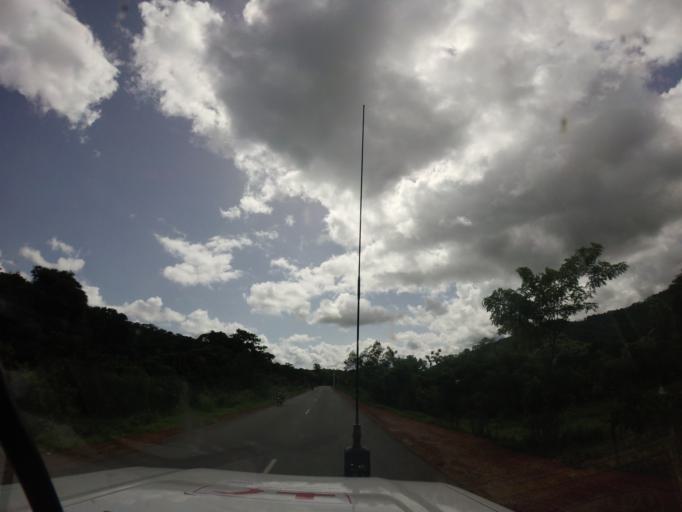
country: GN
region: Mamou
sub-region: Mamou Prefecture
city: Mamou
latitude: 10.2905
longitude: -11.9848
